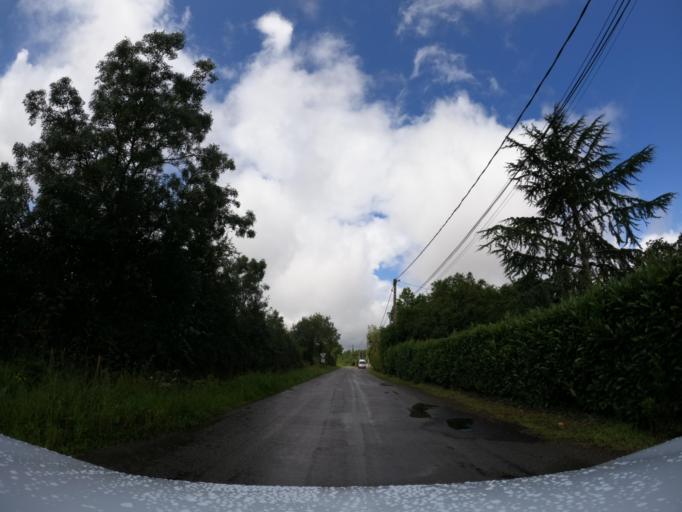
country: FR
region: Pays de la Loire
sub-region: Departement de la Loire-Atlantique
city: Ligne
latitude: 47.3976
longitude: -1.3819
